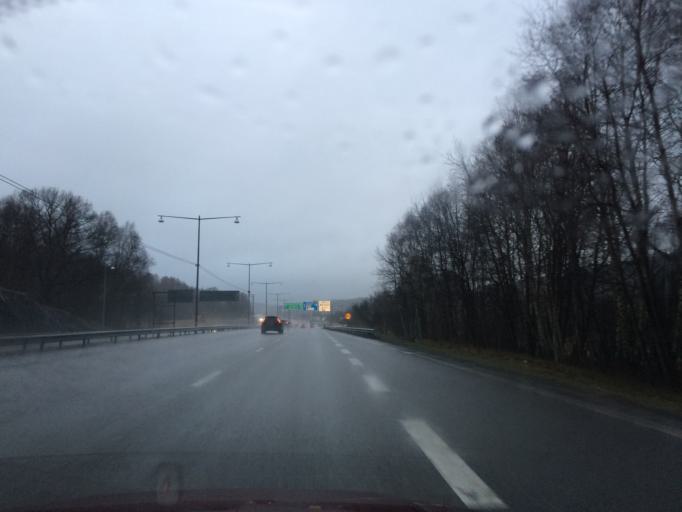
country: SE
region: Vaestra Goetaland
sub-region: Molndal
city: Kallered
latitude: 57.6269
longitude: 12.0359
